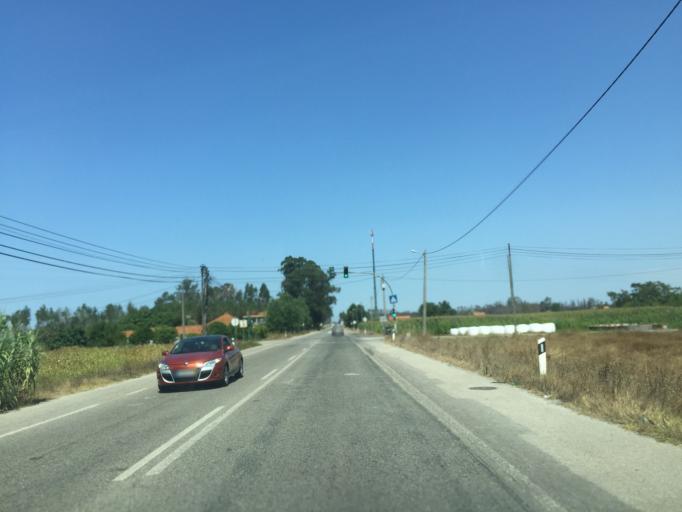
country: PT
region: Coimbra
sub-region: Mira
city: Mira
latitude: 40.3283
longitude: -8.7514
